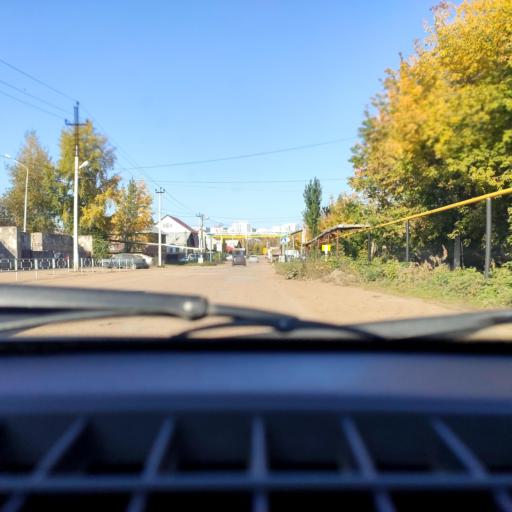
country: RU
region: Bashkortostan
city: Ufa
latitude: 54.7030
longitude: 55.9546
